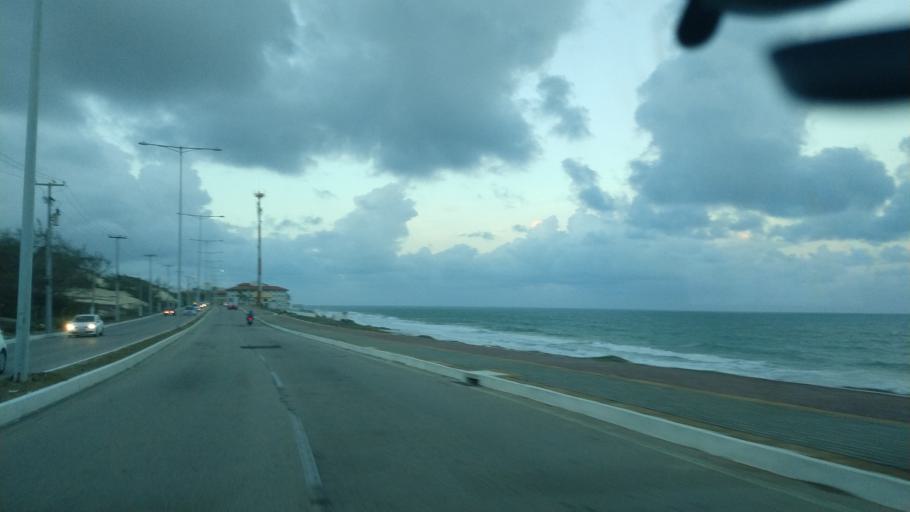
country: BR
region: Rio Grande do Norte
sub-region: Natal
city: Natal
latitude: -5.8141
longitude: -35.1821
